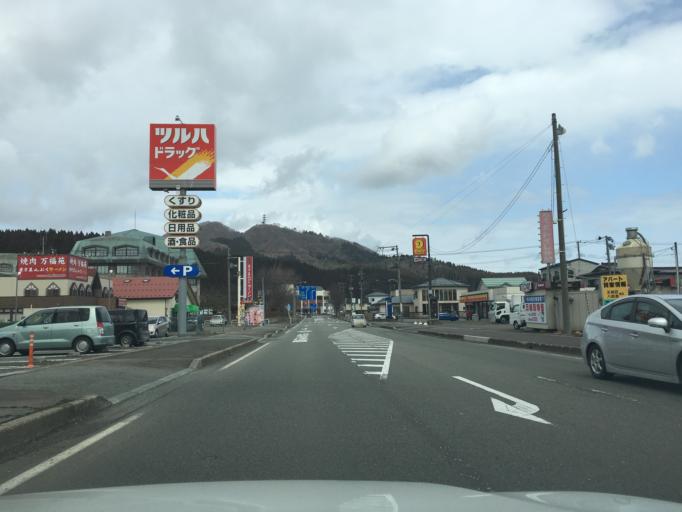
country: JP
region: Akita
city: Tenno
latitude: 39.9422
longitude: 140.1122
